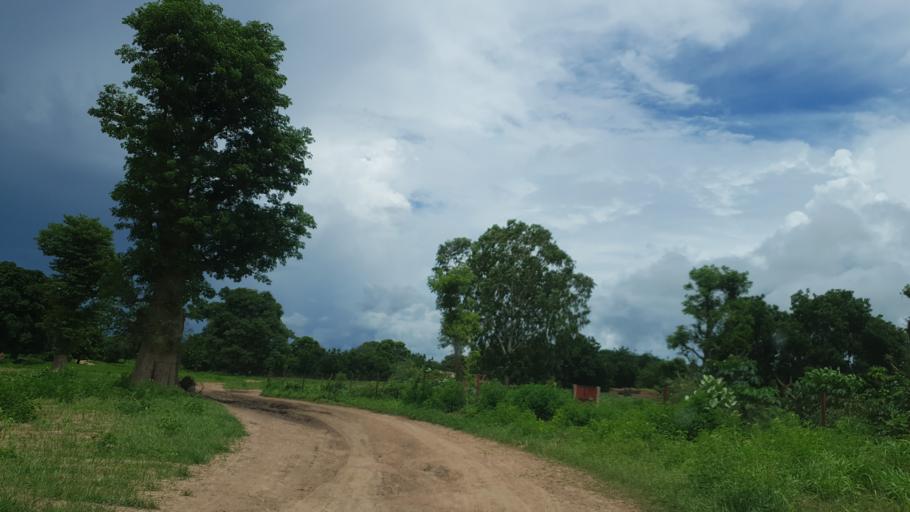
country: ML
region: Koulikoro
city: Kolokani
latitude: 13.5405
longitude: -8.0708
